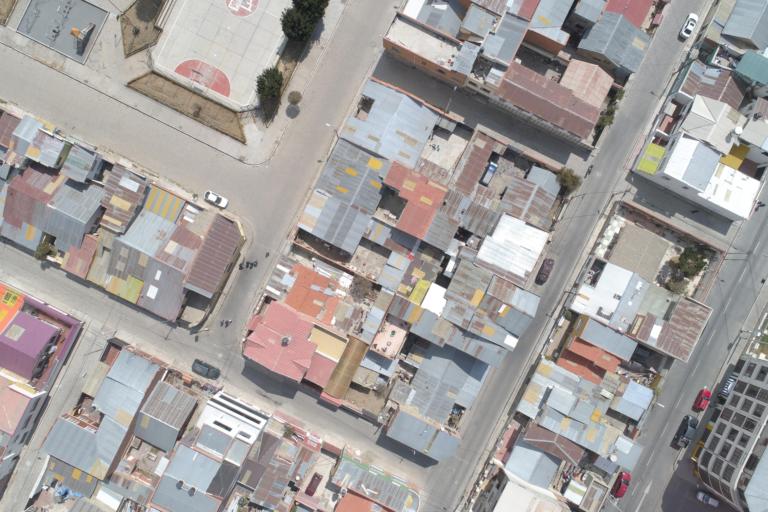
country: BO
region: La Paz
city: La Paz
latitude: -16.5265
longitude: -68.1488
